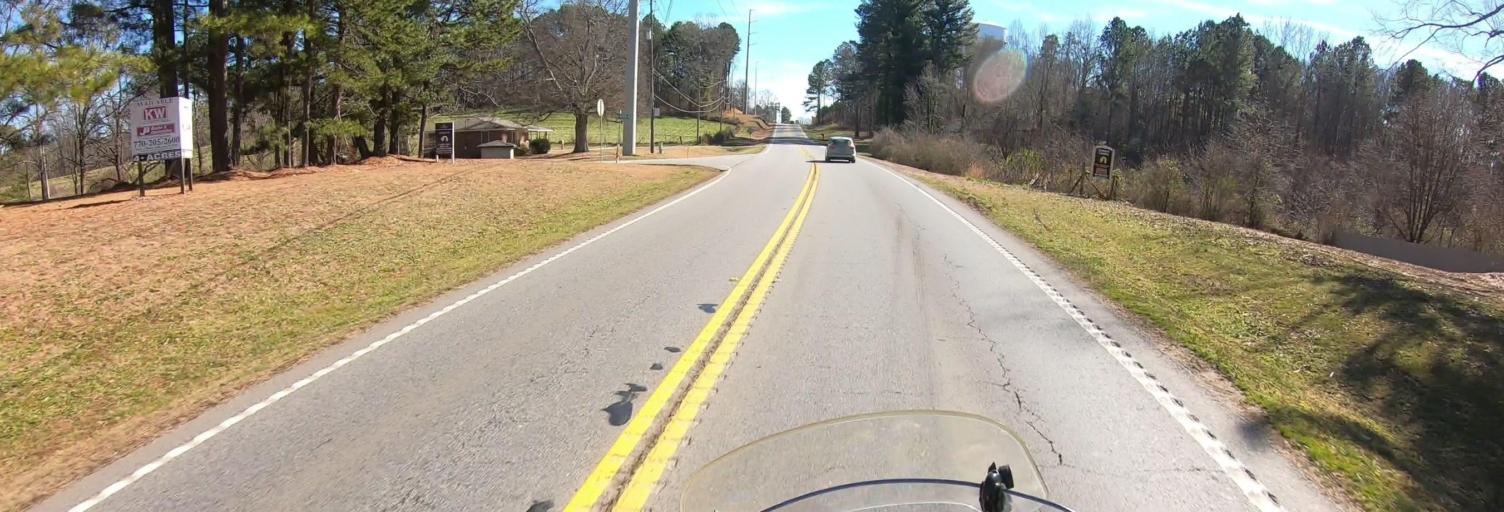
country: US
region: Georgia
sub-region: Forsyth County
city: Cumming
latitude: 34.2845
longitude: -84.1338
